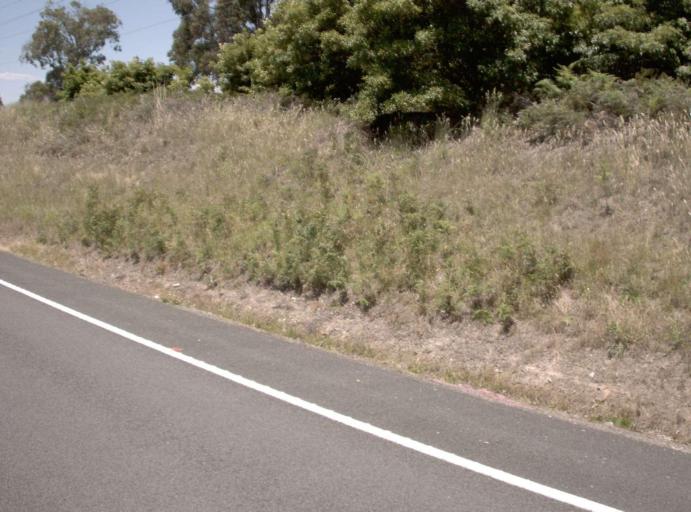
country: AU
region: Victoria
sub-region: East Gippsland
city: Lakes Entrance
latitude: -37.7044
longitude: 148.4733
